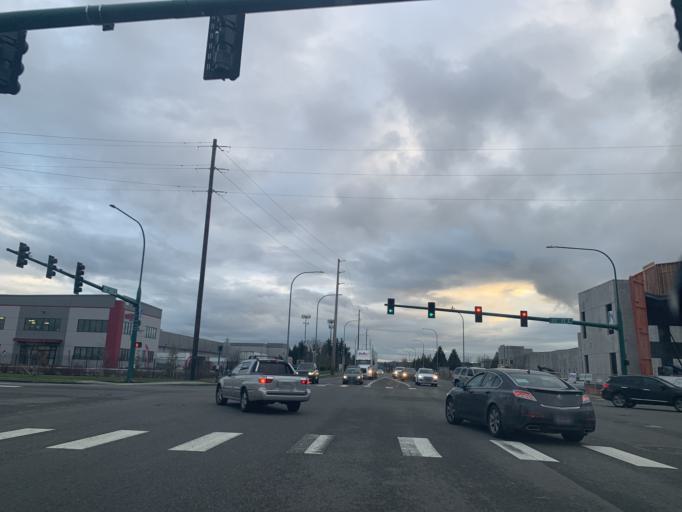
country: US
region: Washington
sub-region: Pierce County
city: Fife
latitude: 47.2393
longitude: -122.3364
